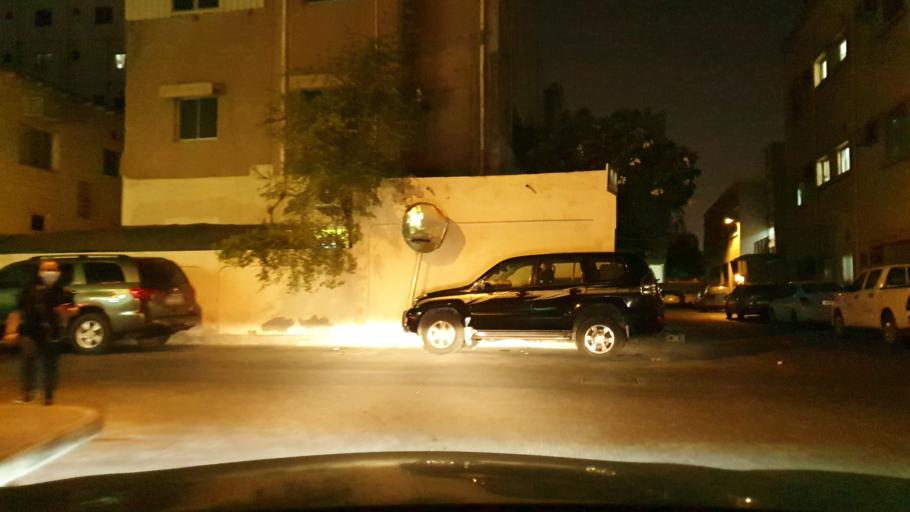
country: BH
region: Manama
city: Manama
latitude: 26.2144
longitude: 50.5866
